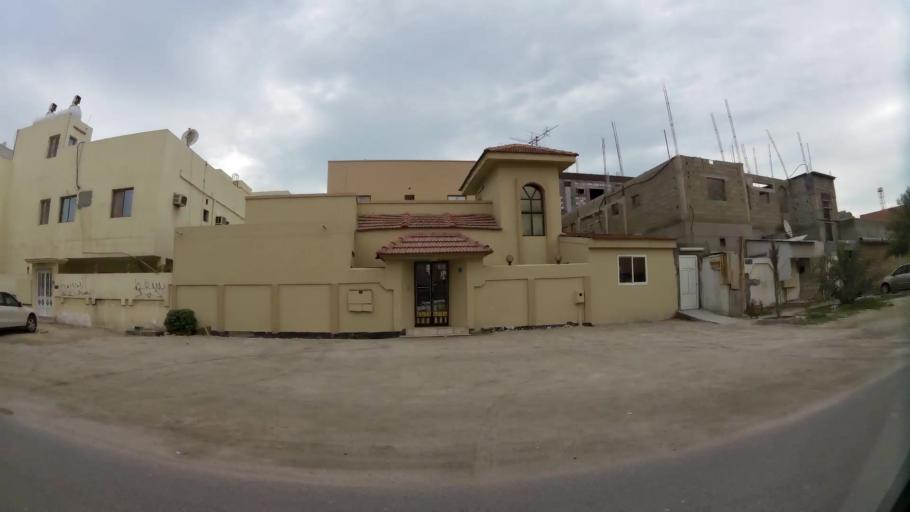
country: BH
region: Northern
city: Sitrah
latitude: 26.1680
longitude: 50.6075
